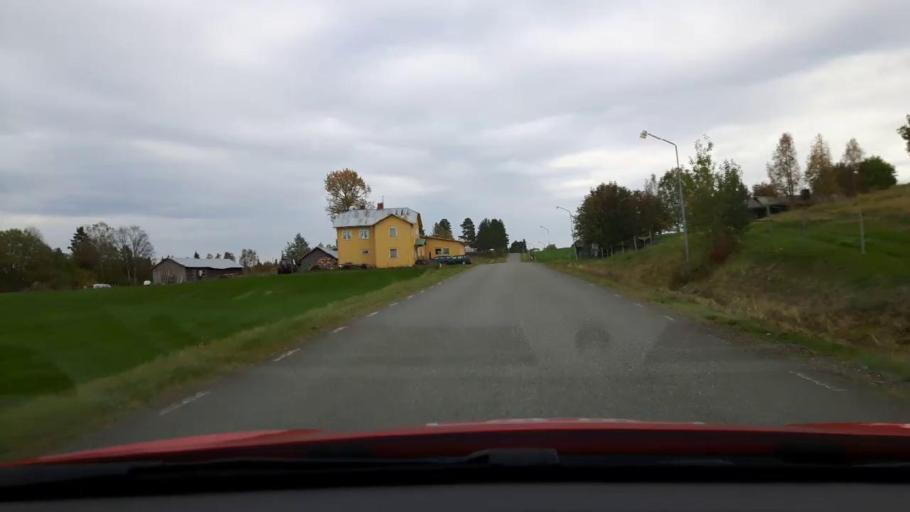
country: SE
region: Jaemtland
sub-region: Krokoms Kommun
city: Krokom
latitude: 63.2311
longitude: 14.1260
